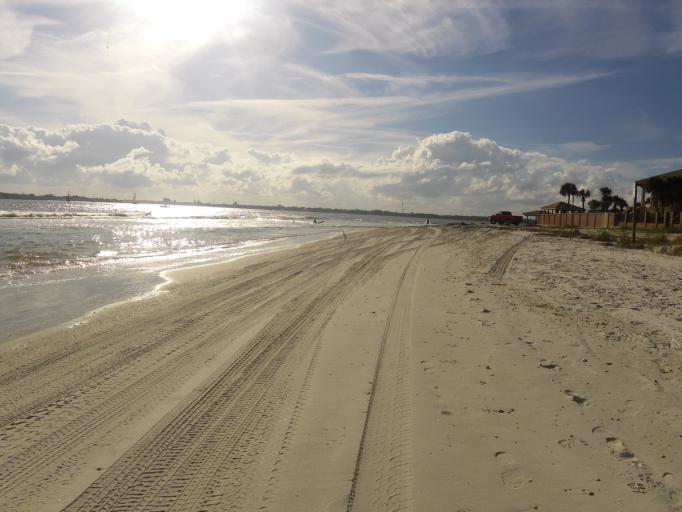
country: US
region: Florida
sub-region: Saint Johns County
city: Saint Augustine
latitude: 29.9107
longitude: -81.2938
